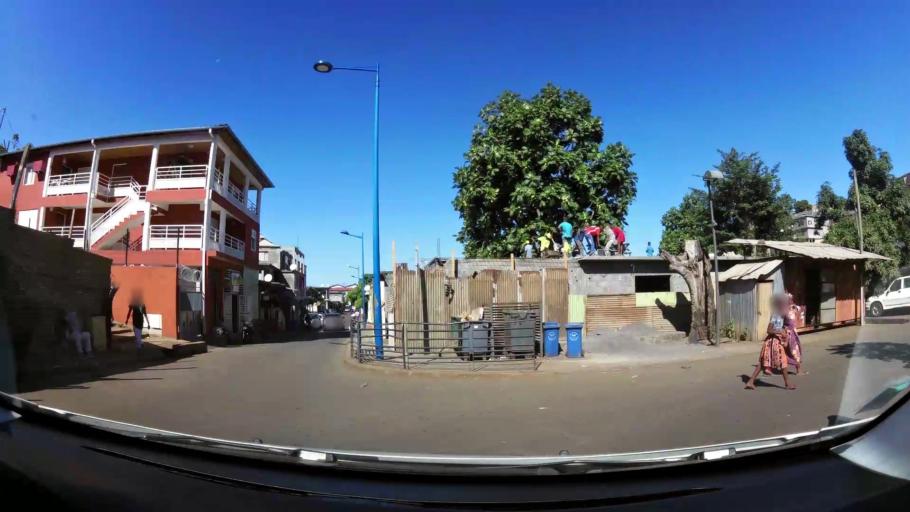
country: YT
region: Mamoudzou
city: Mamoudzou
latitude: -12.7877
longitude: 45.2186
